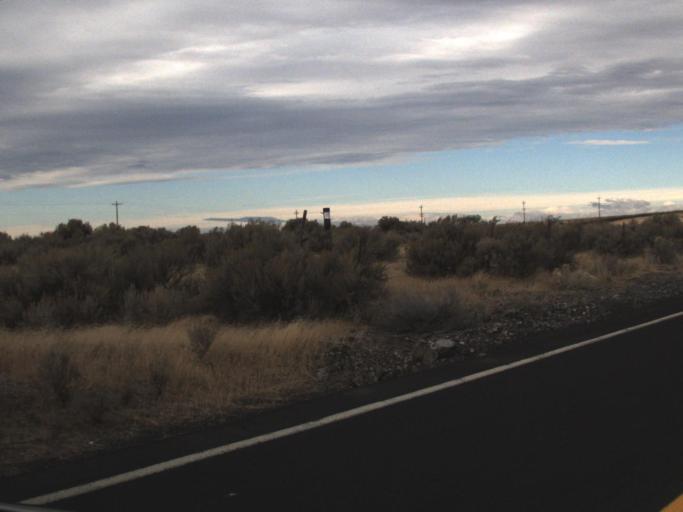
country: US
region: Washington
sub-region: Adams County
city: Ritzville
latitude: 47.4256
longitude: -118.7056
